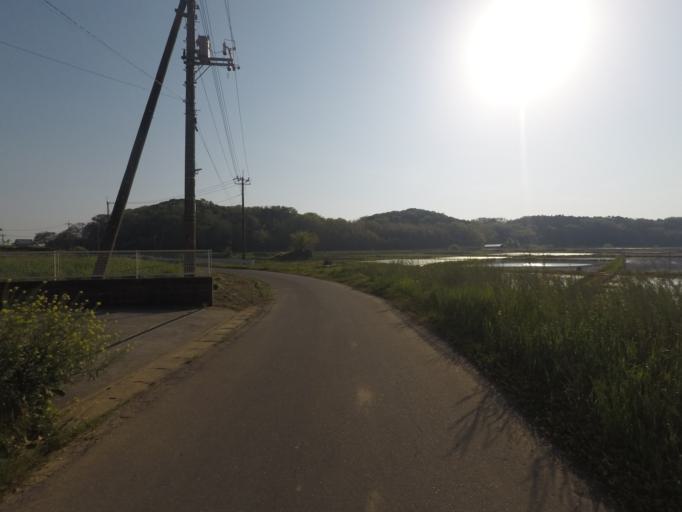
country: JP
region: Ibaraki
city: Inashiki
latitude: 36.0681
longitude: 140.3592
